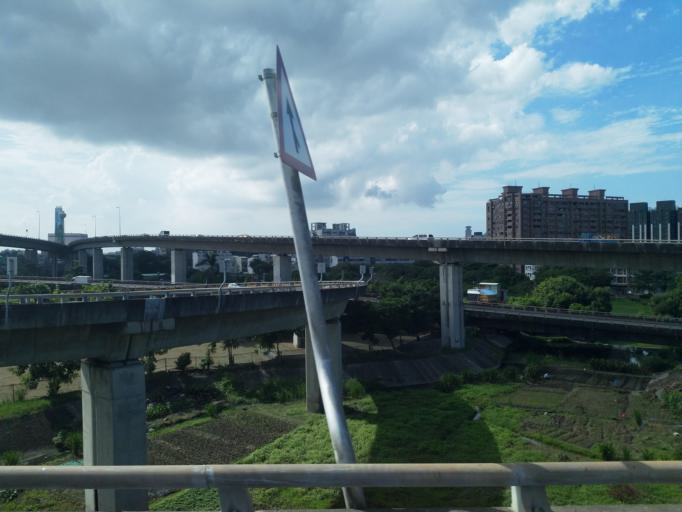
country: TW
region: Taiwan
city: Fengshan
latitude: 22.6752
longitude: 120.3275
